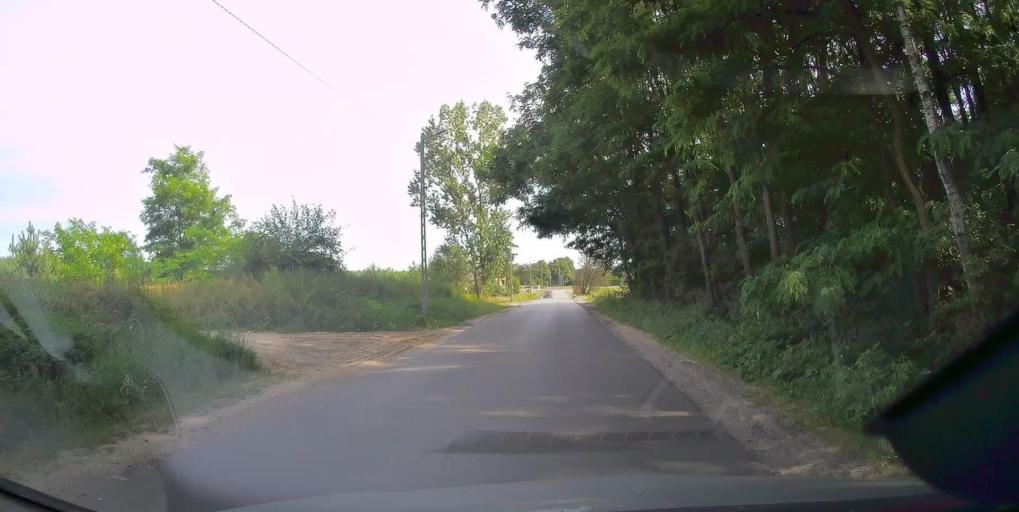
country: PL
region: Lodz Voivodeship
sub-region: Powiat tomaszowski
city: Tomaszow Mazowiecki
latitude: 51.4590
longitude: 20.0344
